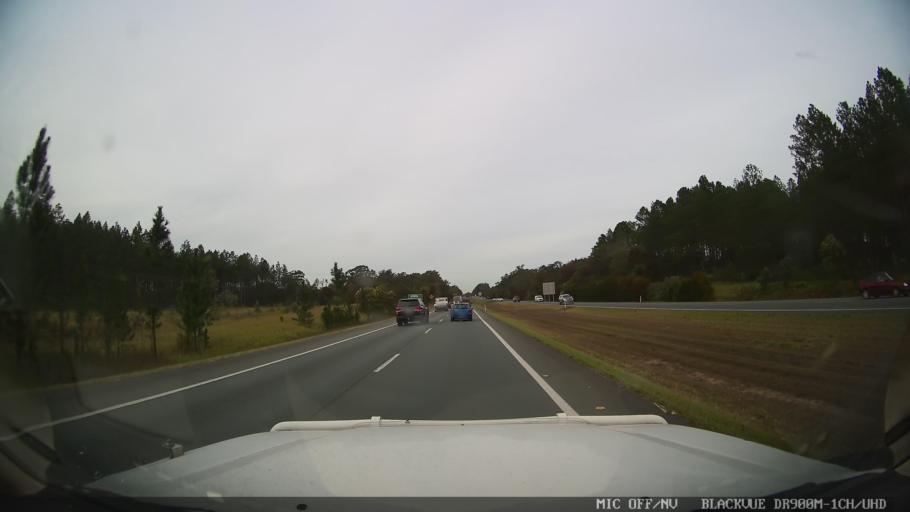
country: AU
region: Queensland
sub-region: Moreton Bay
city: Caboolture
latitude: -26.9927
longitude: 152.9779
